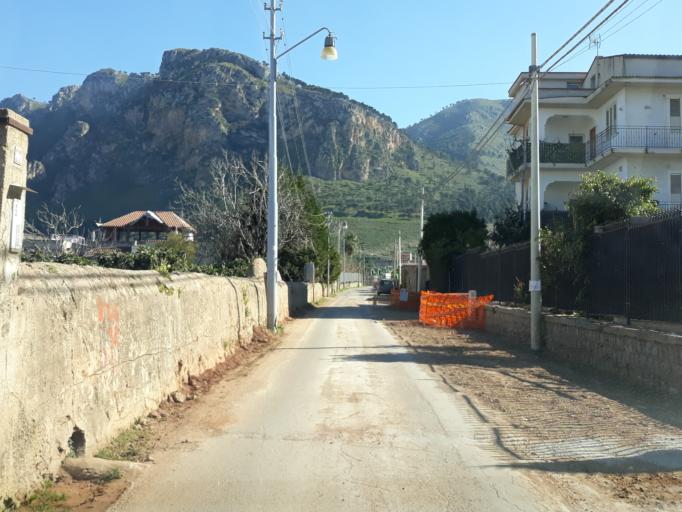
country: IT
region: Sicily
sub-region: Palermo
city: Villa Ciambra
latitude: 38.0806
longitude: 13.3466
